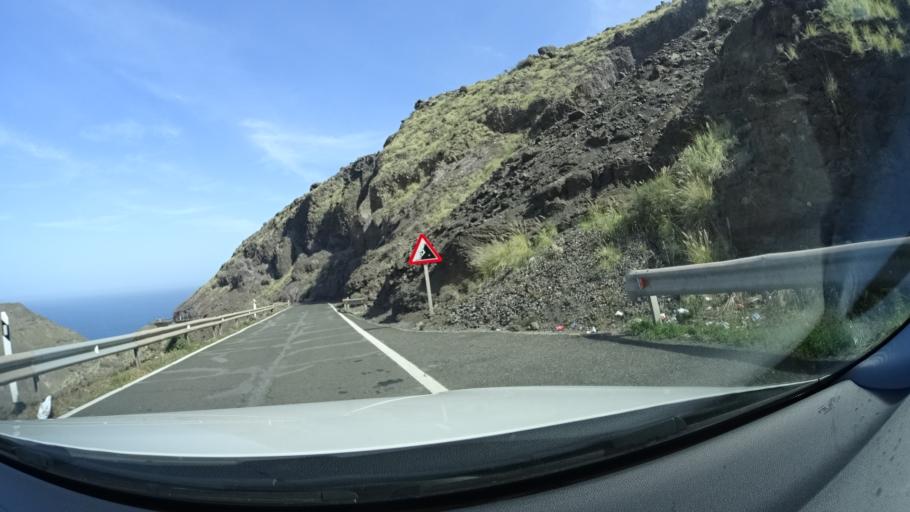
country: ES
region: Canary Islands
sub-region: Provincia de Las Palmas
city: Agaete
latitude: 28.0446
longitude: -15.7348
